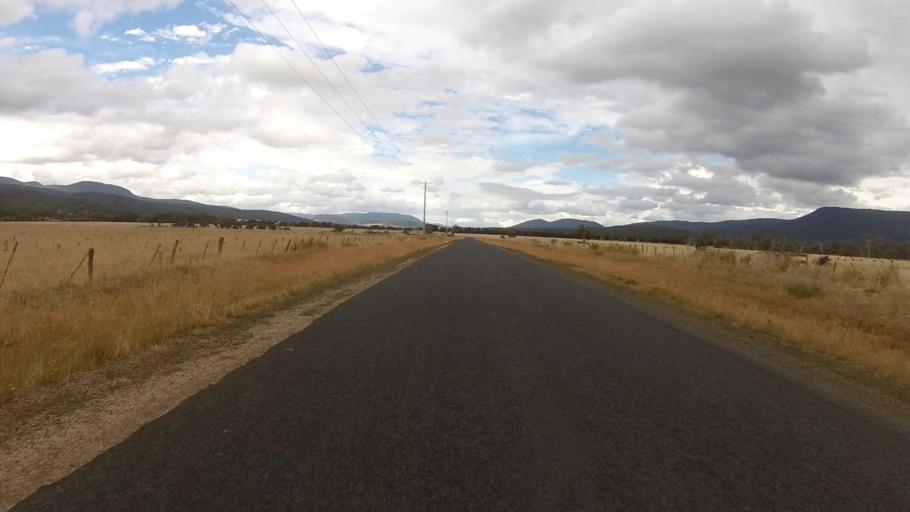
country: AU
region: Tasmania
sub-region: Break O'Day
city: St Helens
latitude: -41.8246
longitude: 147.8549
